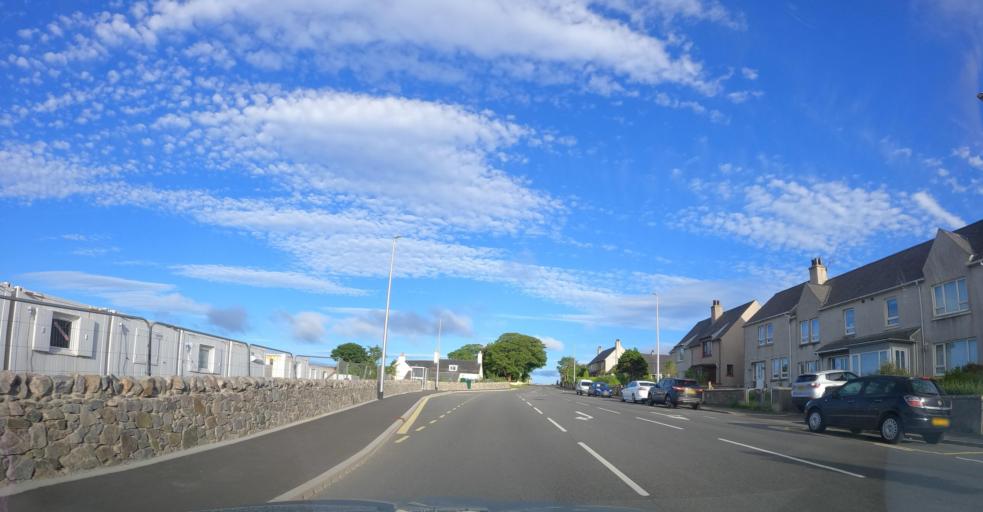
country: GB
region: Scotland
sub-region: Eilean Siar
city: Isle of Lewis
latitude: 58.2166
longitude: -6.3742
